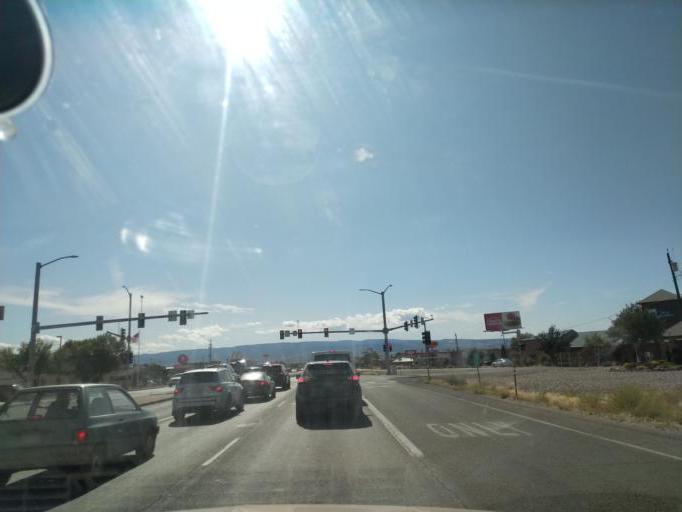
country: US
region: Colorado
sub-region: Mesa County
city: Clifton
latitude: 39.0910
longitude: -108.4545
